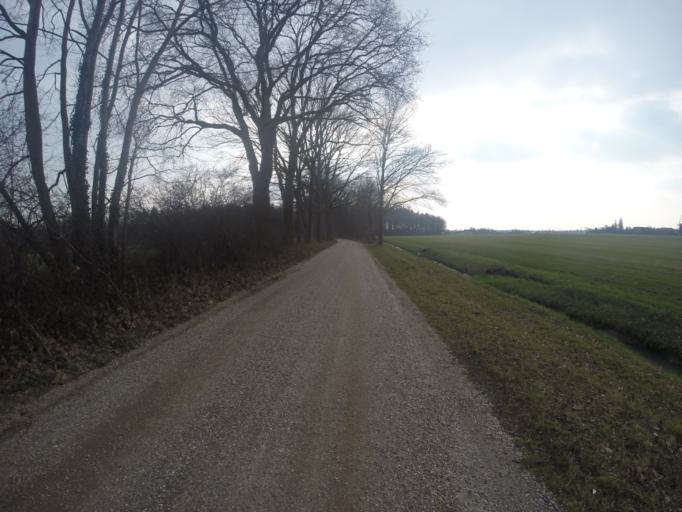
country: NL
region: Gelderland
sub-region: Gemeente Lochem
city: Almen
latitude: 52.1469
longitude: 6.2845
